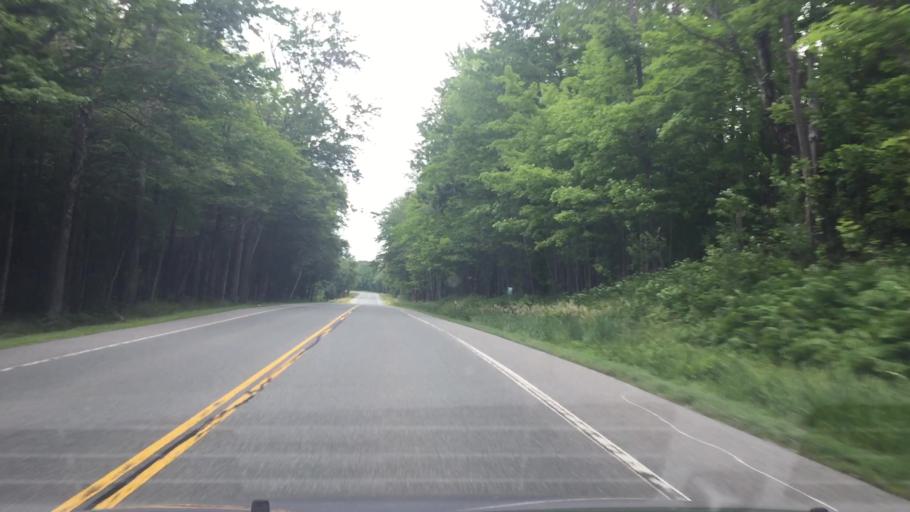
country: US
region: New Hampshire
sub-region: Grafton County
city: Deerfield
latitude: 44.2150
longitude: -71.6764
